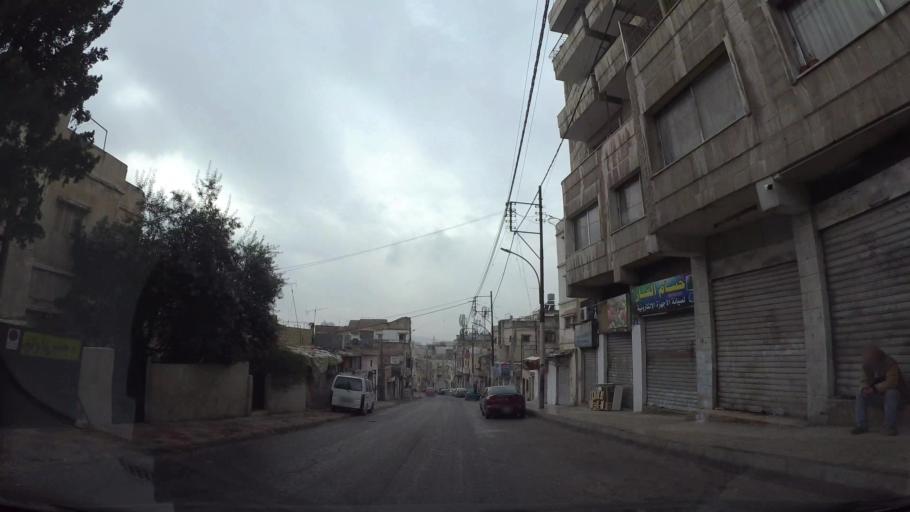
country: JO
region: Amman
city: Amman
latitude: 31.9662
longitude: 35.9288
